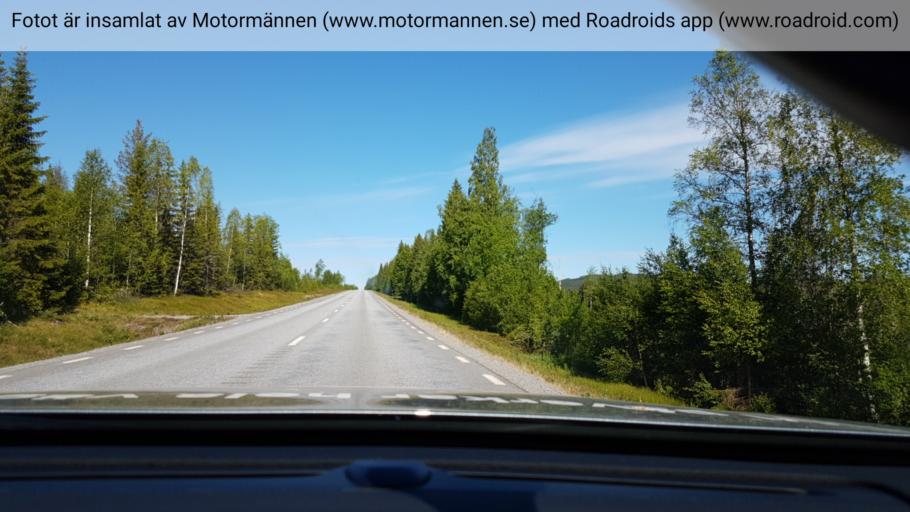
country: SE
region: Vaesterbotten
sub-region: Bjurholms Kommun
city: Bjurholm
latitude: 63.9451
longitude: 18.9137
